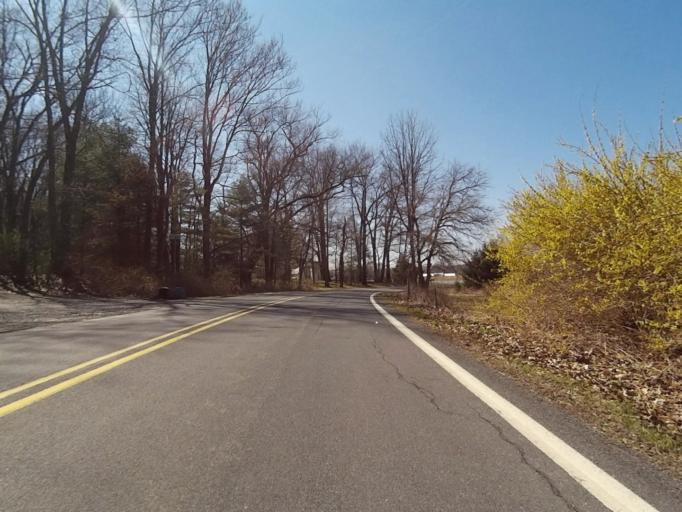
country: US
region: Pennsylvania
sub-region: Centre County
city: Stormstown
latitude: 40.7479
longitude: -77.9985
